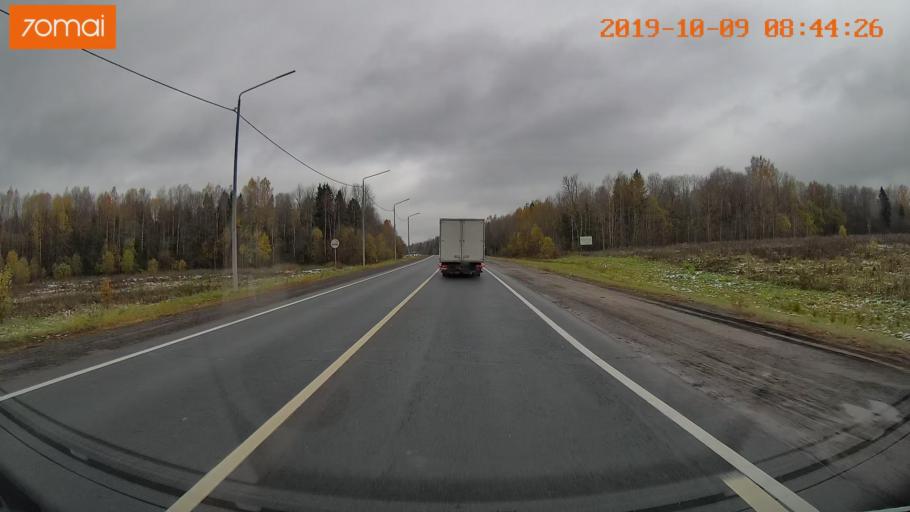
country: RU
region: Vologda
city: Gryazovets
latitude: 59.0366
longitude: 40.1078
